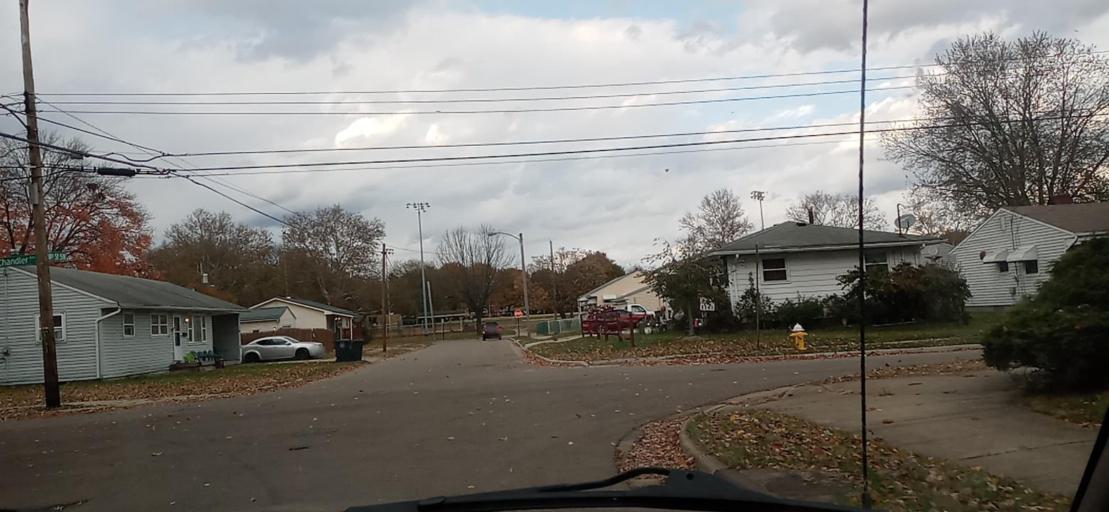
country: US
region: Ohio
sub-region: Summit County
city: Barberton
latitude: 41.0457
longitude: -81.5685
